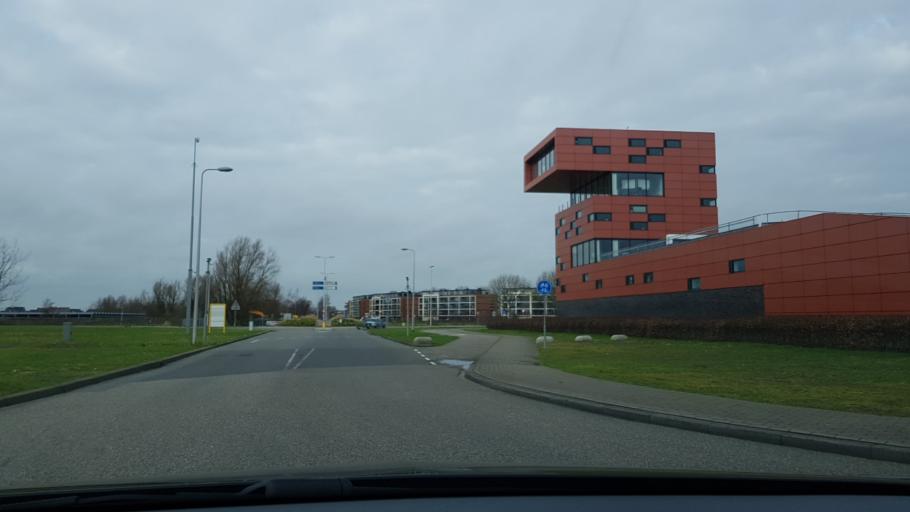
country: NL
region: South Holland
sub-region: Gemeente Alphen aan den Rijn
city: Alphen aan den Rijn
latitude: 52.1119
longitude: 4.6608
